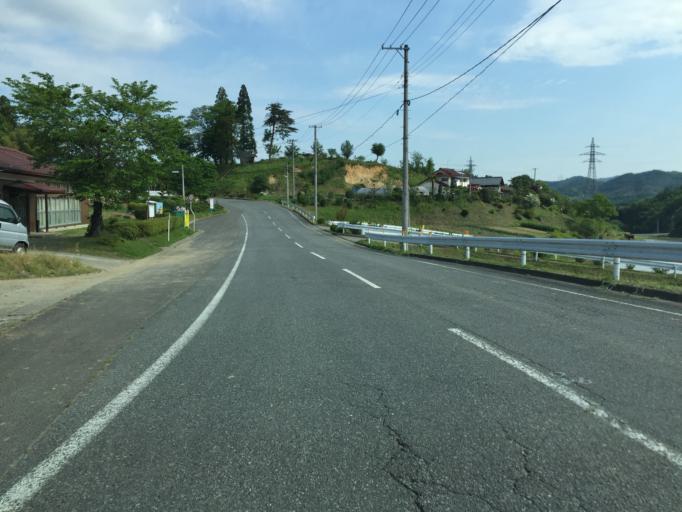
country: JP
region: Fukushima
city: Fukushima-shi
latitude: 37.6622
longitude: 140.4961
